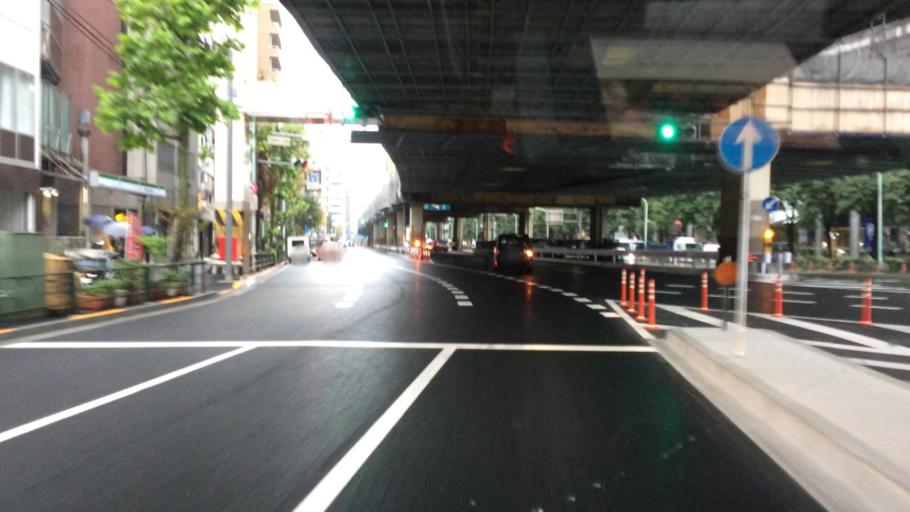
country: JP
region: Tokyo
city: Tokyo
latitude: 35.6670
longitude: 139.7387
